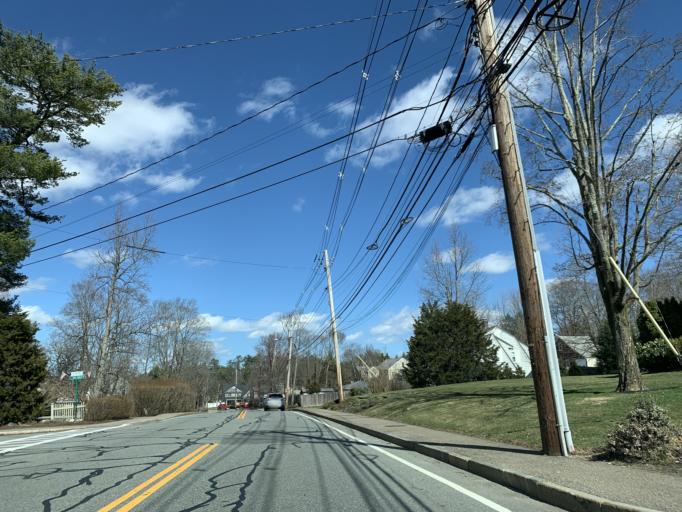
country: US
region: Massachusetts
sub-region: Norfolk County
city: Canton
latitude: 42.1831
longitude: -71.1252
